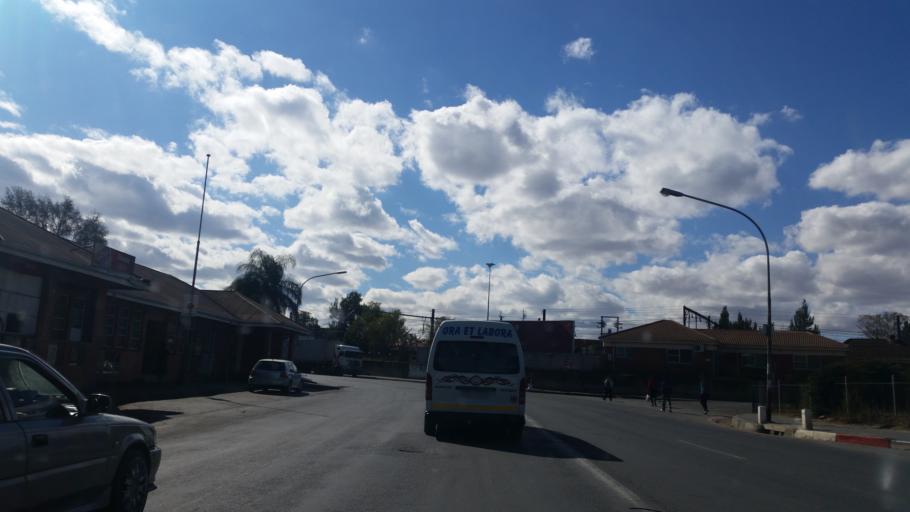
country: ZA
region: KwaZulu-Natal
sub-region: uThukela District Municipality
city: Ladysmith
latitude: -28.5579
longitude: 29.7849
